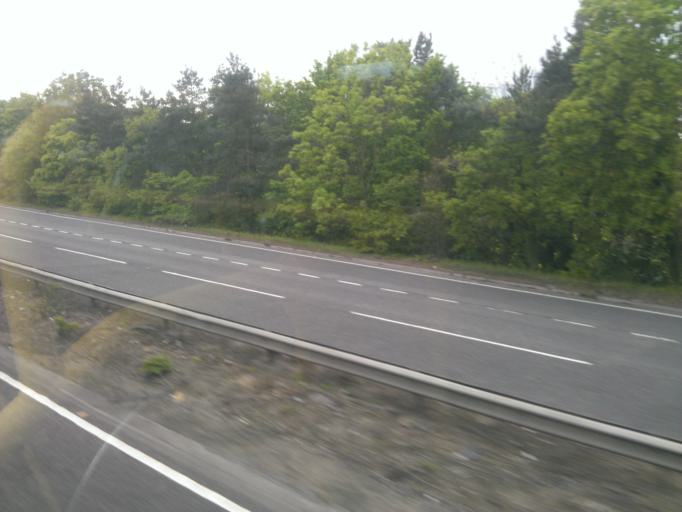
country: GB
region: England
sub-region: Essex
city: Colchester
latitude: 51.9287
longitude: 0.9429
